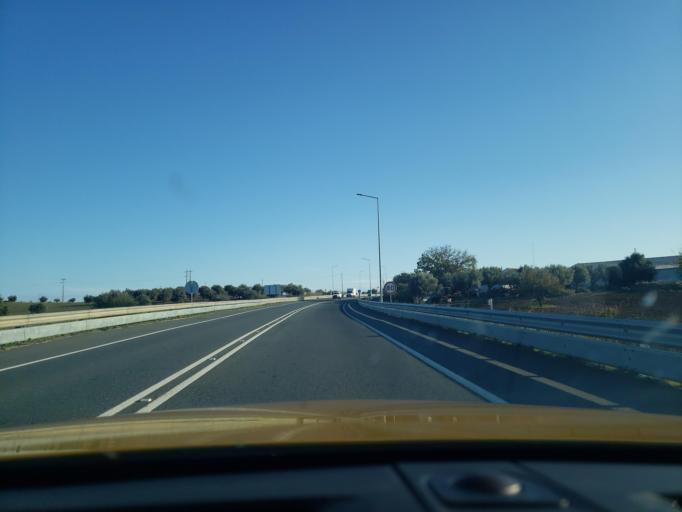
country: PT
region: Evora
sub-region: Portel
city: Portel
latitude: 38.4595
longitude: -7.7462
